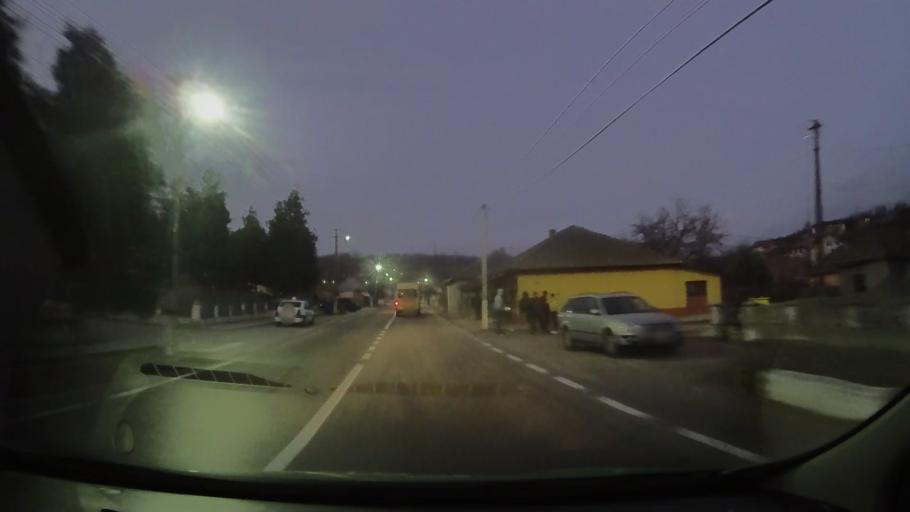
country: RO
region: Constanta
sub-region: Comuna Ion Corvin
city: Ion Corvin
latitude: 44.1129
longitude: 27.8061
